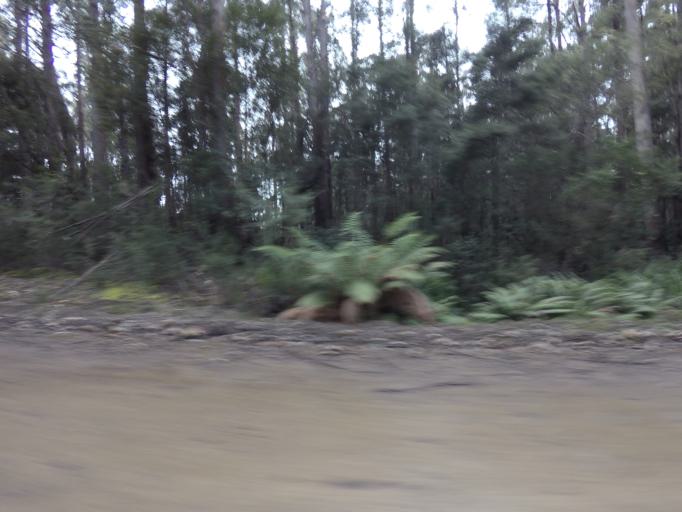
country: AU
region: Tasmania
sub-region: Huon Valley
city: Geeveston
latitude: -43.4801
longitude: 146.8907
